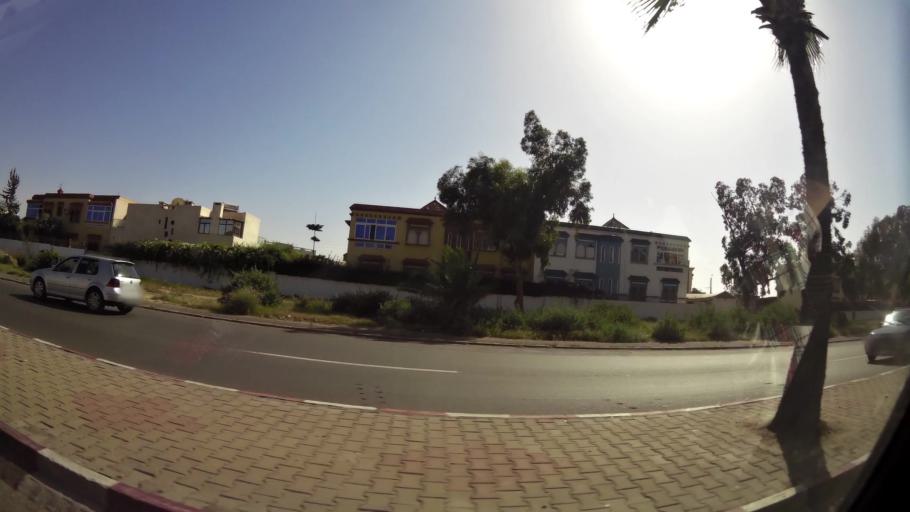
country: MA
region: Souss-Massa-Draa
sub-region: Inezgane-Ait Mellou
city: Inezgane
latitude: 30.3780
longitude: -9.5604
